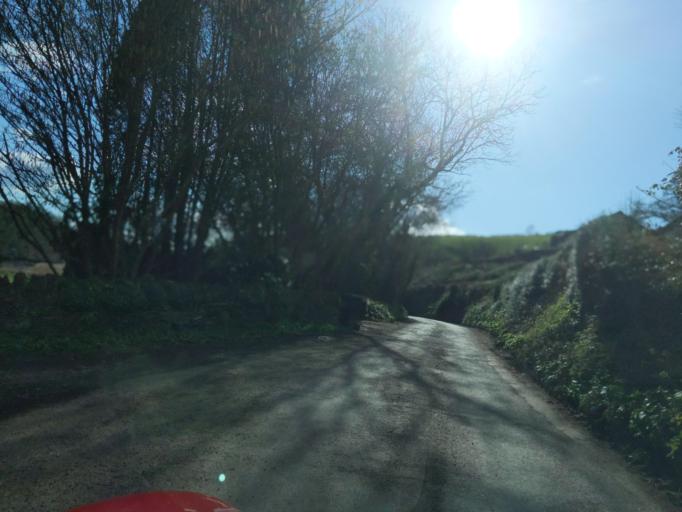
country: GB
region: England
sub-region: Devon
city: Kingsbridge
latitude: 50.2849
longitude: -3.7584
